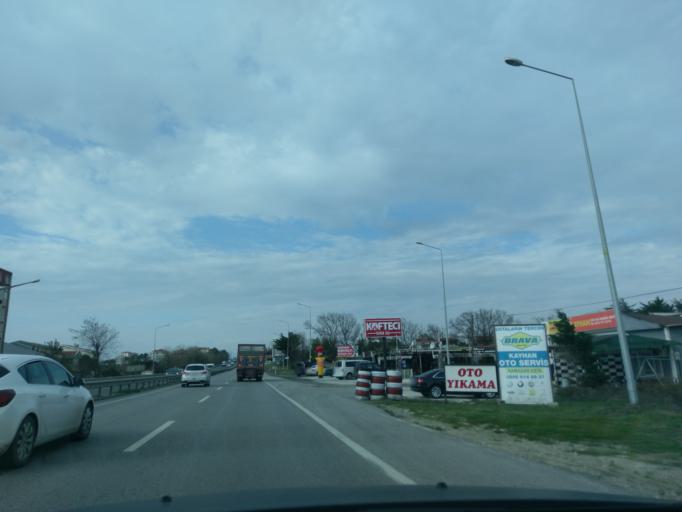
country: TR
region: Istanbul
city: Celaliye
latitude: 41.0478
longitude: 28.4002
